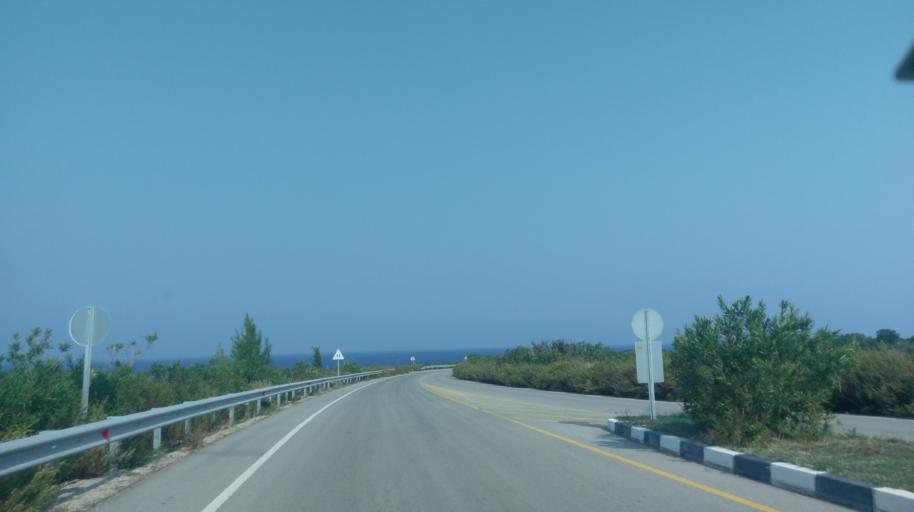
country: CY
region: Ammochostos
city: Trikomo
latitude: 35.4381
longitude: 33.9508
